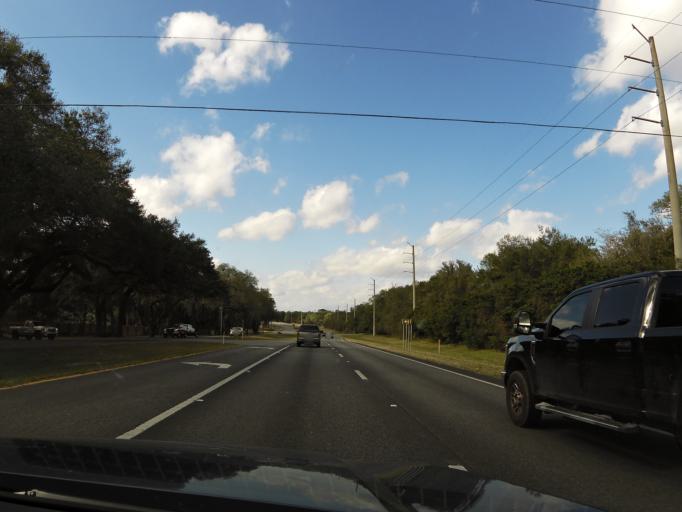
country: US
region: Florida
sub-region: Volusia County
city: North DeLand
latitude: 29.0825
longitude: -81.3184
